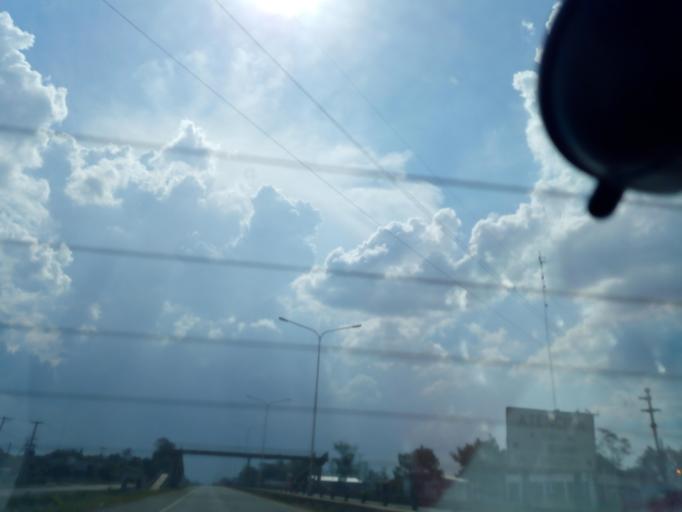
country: AR
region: Corrientes
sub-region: Departamento de Paso de los Libres
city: Paso de los Libres
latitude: -29.7220
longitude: -57.1386
